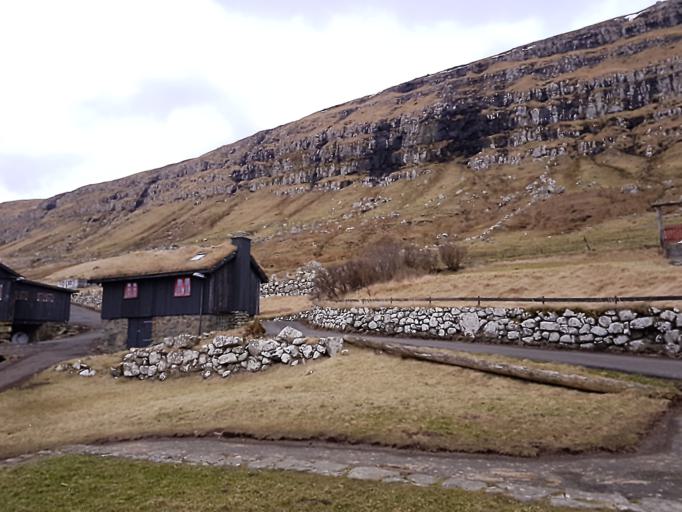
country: FO
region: Streymoy
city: Argir
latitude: 61.9522
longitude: -6.7923
